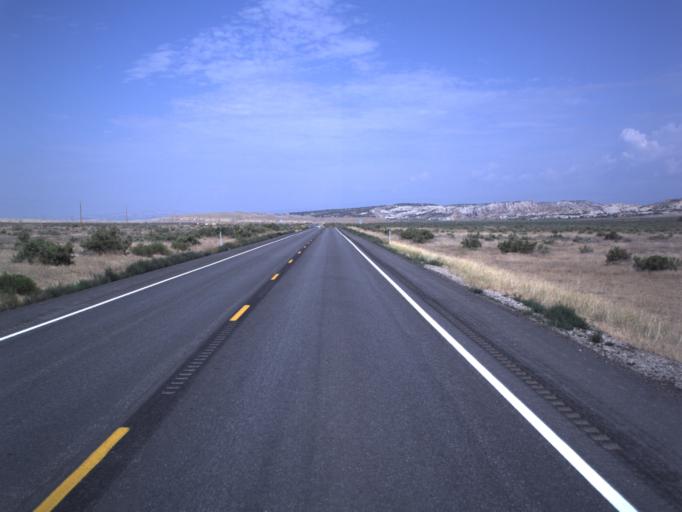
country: US
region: Utah
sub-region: Uintah County
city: Naples
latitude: 40.3039
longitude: -109.2035
